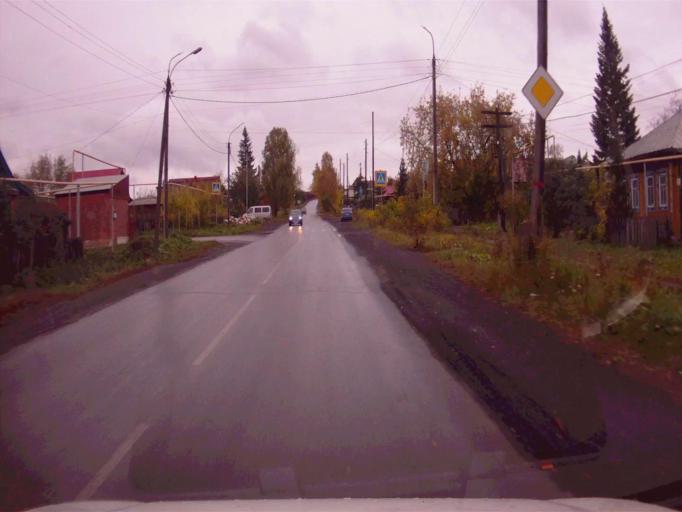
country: RU
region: Chelyabinsk
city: Verkhniy Ufaley
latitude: 56.0491
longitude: 60.2069
